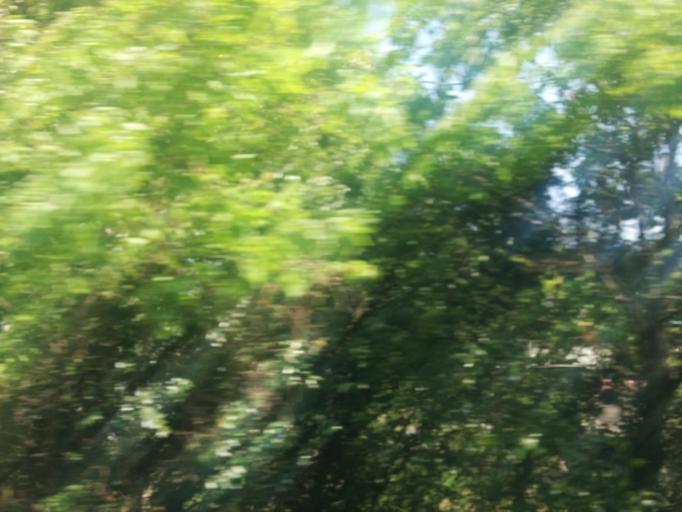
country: JP
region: Osaka
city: Kashihara
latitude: 34.5539
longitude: 135.6717
